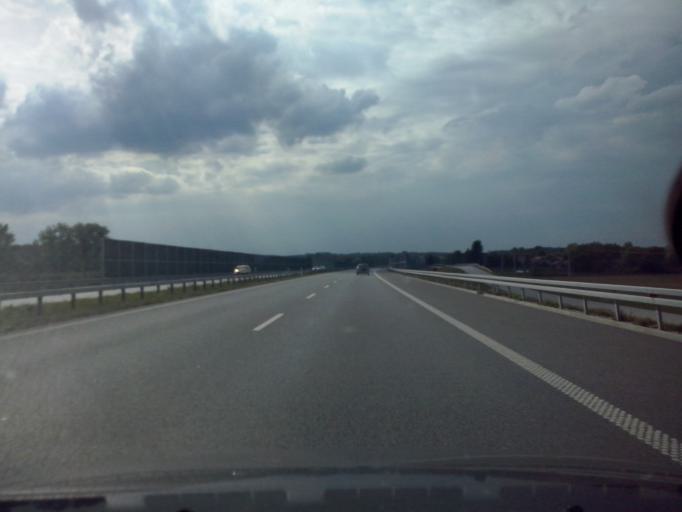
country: PL
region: Lesser Poland Voivodeship
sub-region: Powiat brzeski
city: Maszkienice
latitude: 50.0041
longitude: 20.7133
